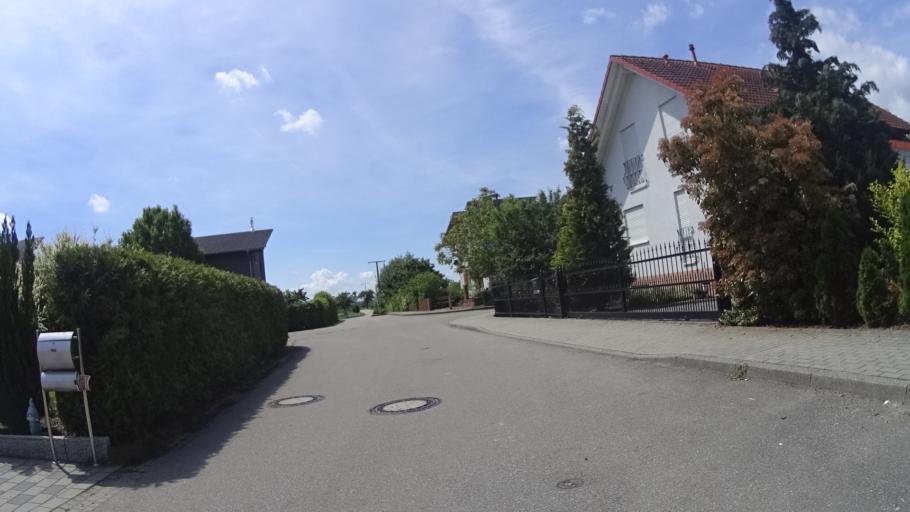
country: DE
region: Baden-Wuerttemberg
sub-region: Freiburg Region
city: Schwanau
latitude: 48.3797
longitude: 7.7540
